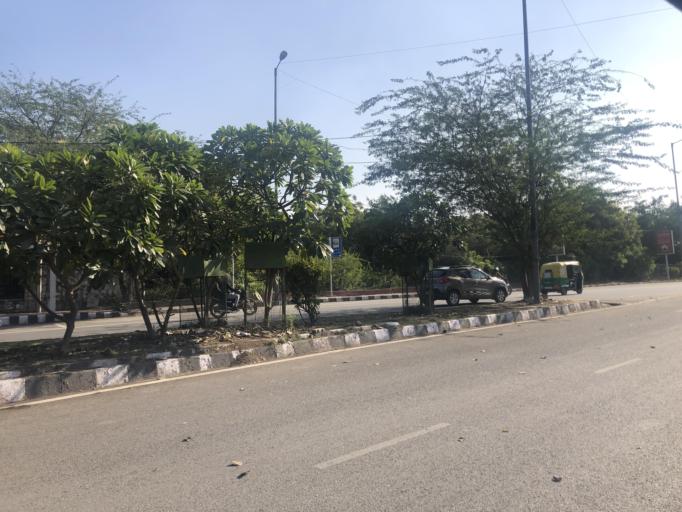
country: IN
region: NCT
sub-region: Central Delhi
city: Karol Bagh
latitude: 28.5523
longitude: 77.1654
